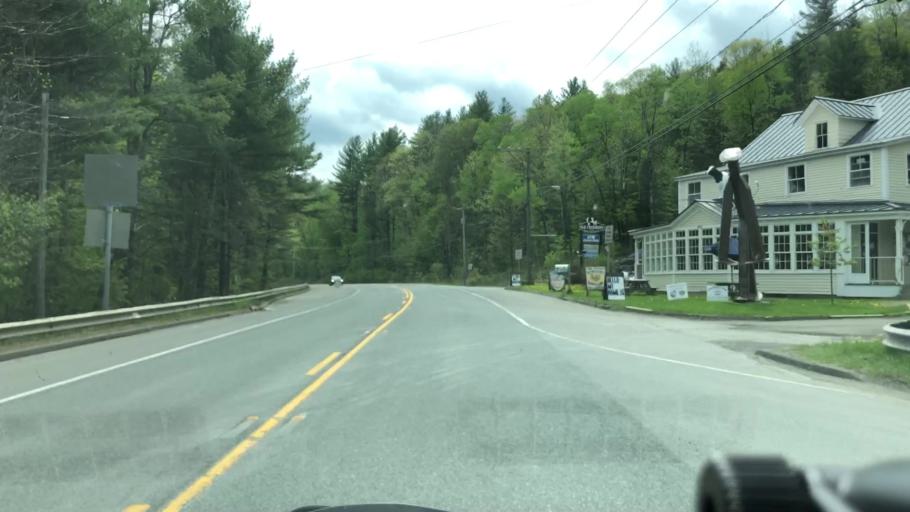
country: US
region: Massachusetts
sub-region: Hampshire County
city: Chesterfield
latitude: 42.4644
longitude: -72.9052
